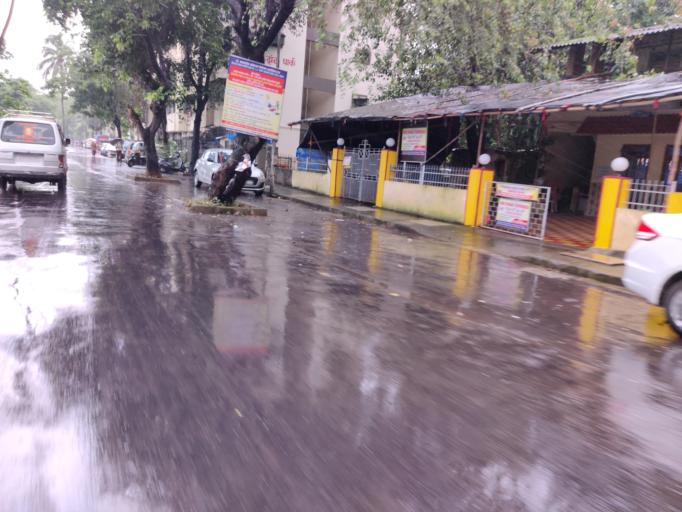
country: IN
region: Maharashtra
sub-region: Mumbai Suburban
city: Borivli
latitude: 19.2545
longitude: 72.8561
